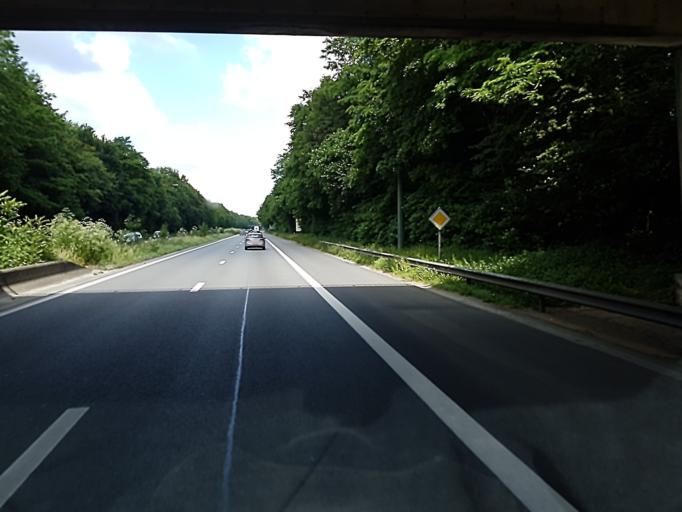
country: BE
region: Wallonia
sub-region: Province du Brabant Wallon
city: Braine-l'Alleud
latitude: 50.6745
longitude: 4.3942
